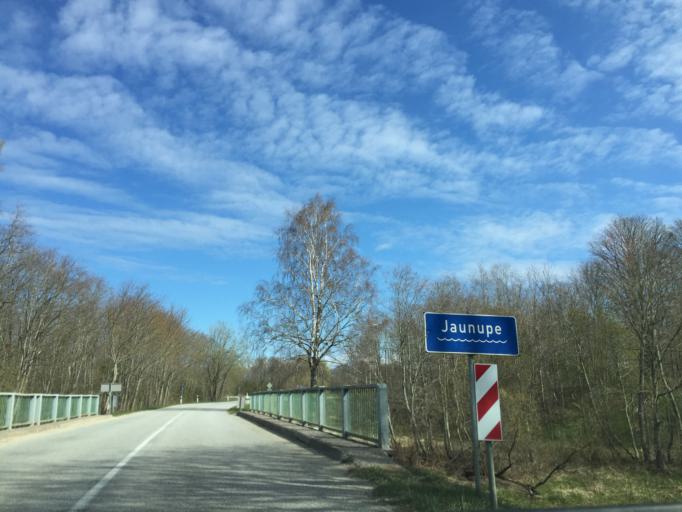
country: LV
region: Salacgrivas
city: Salacgriva
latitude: 57.7484
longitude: 24.4012
